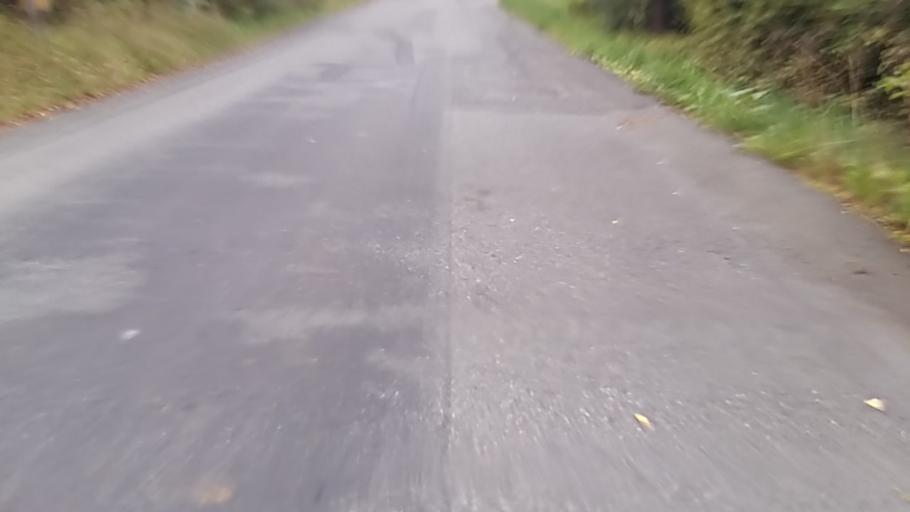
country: SE
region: Joenkoeping
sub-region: Jonkopings Kommun
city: Taberg
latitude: 57.7061
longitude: 14.1117
